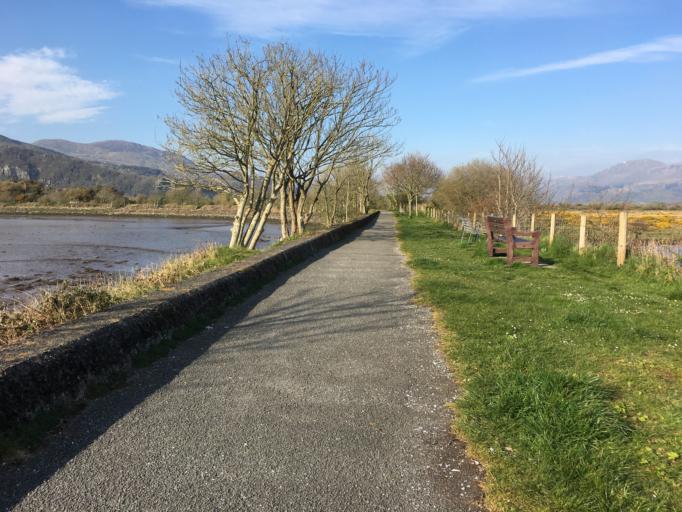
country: GB
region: Wales
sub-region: Gwynedd
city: Porthmadog
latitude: 52.9262
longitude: -4.1241
